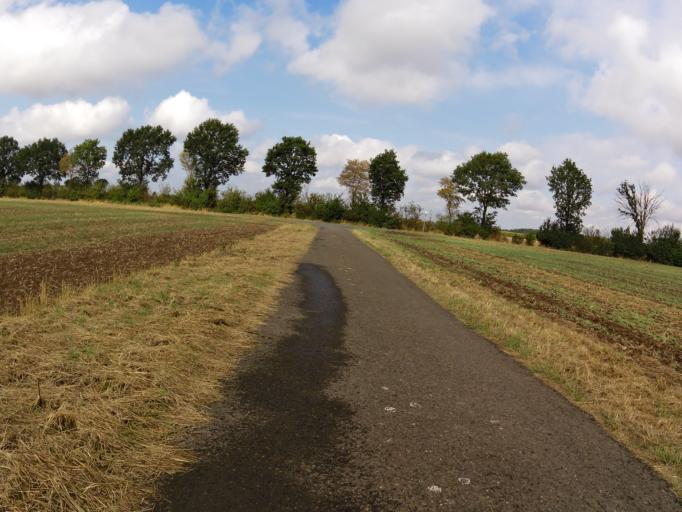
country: DE
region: Lower Saxony
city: Schweringen
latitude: 52.7610
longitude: 9.1731
